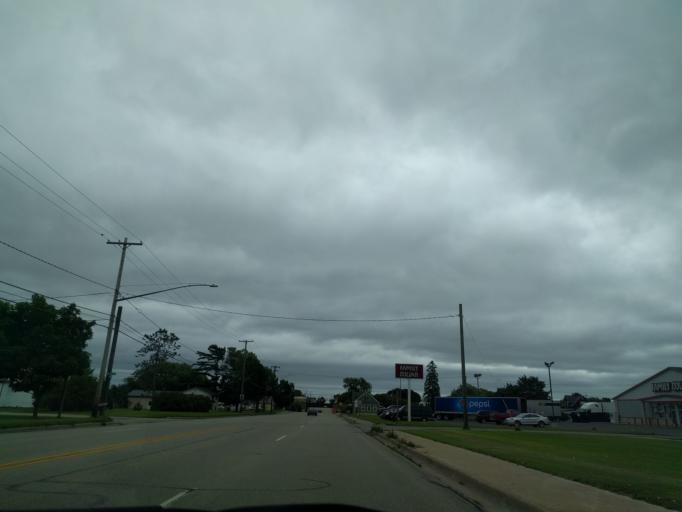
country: US
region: Michigan
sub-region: Delta County
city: Gladstone
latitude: 45.8527
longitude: -87.0290
